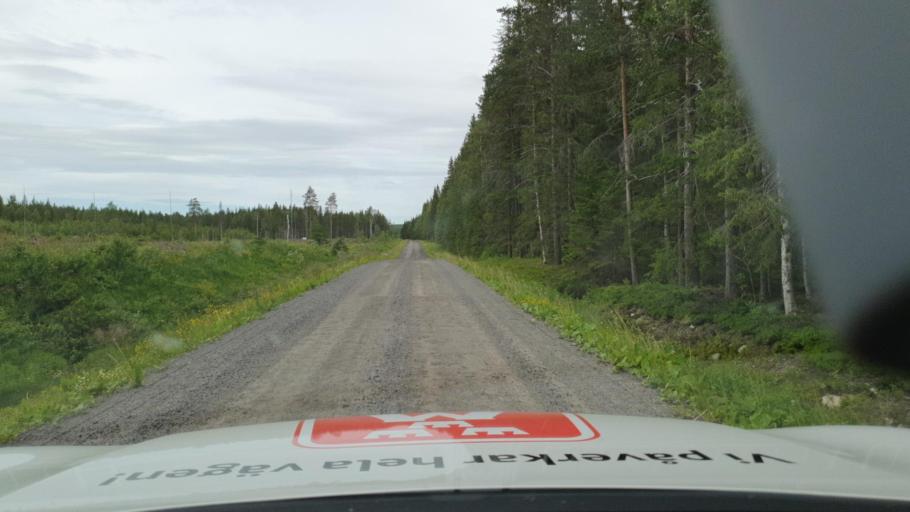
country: SE
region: Vaesterbotten
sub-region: Skelleftea Kommun
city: Burtraesk
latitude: 64.3799
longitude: 20.6148
